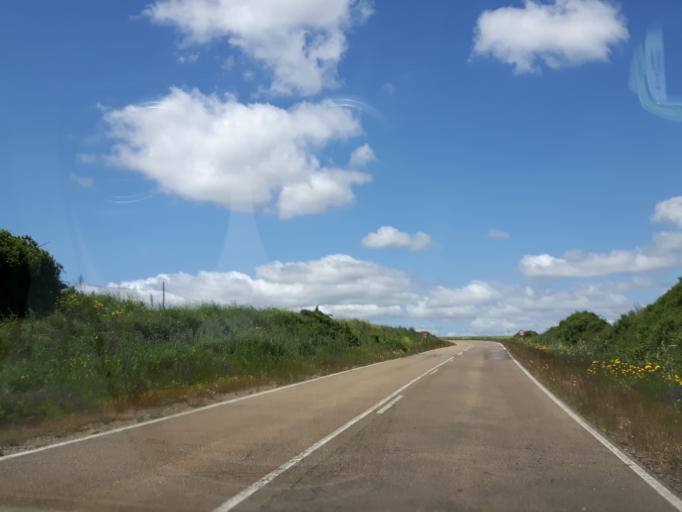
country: ES
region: Castille and Leon
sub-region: Provincia de Salamanca
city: Villar de Ciervo
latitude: 40.7263
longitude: -6.7554
